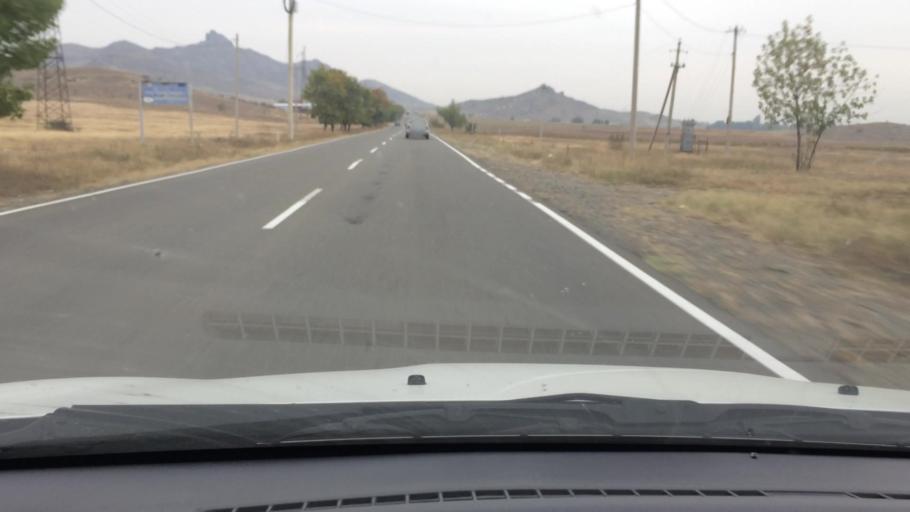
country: GE
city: Naghvarevi
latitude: 41.3388
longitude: 44.8106
